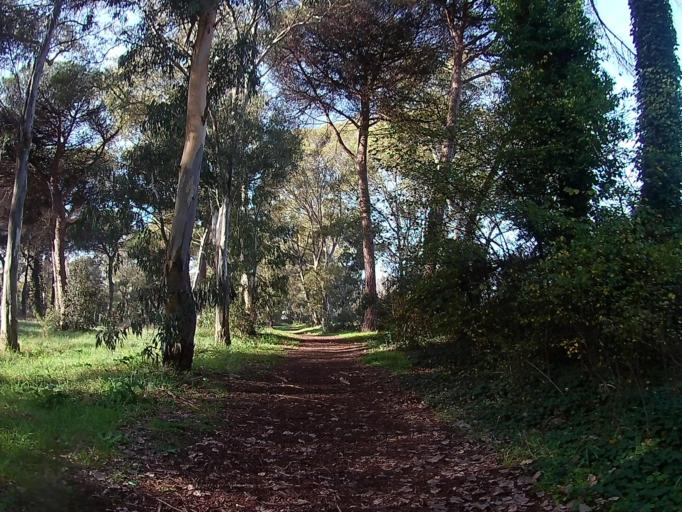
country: IT
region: Latium
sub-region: Citta metropolitana di Roma Capitale
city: Lido di Ostia
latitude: 41.7465
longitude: 12.2779
